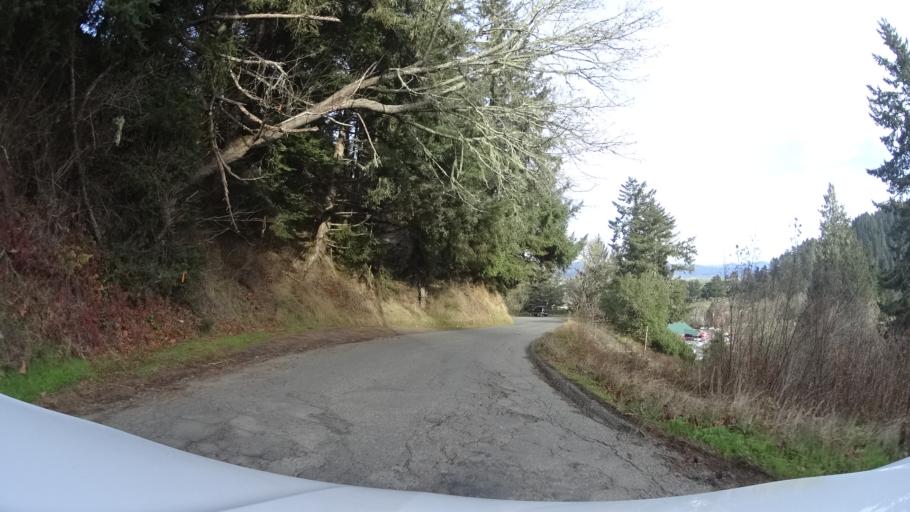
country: US
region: California
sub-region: Humboldt County
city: Ferndale
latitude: 40.5737
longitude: -124.2688
